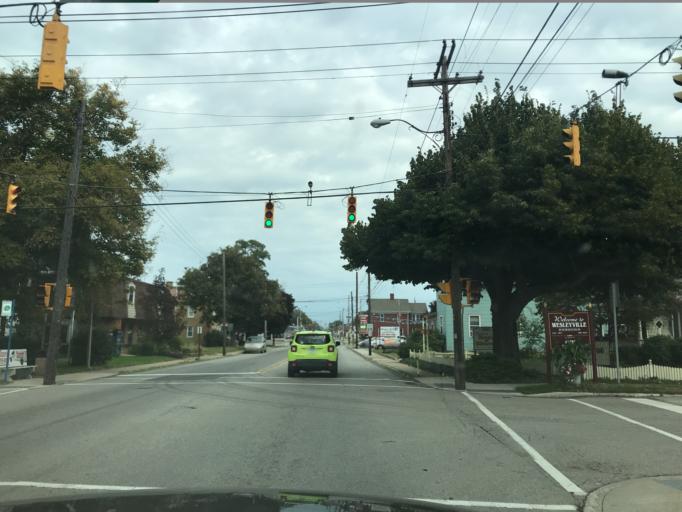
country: US
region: Pennsylvania
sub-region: Erie County
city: Wesleyville
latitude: 42.1381
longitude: -80.0197
